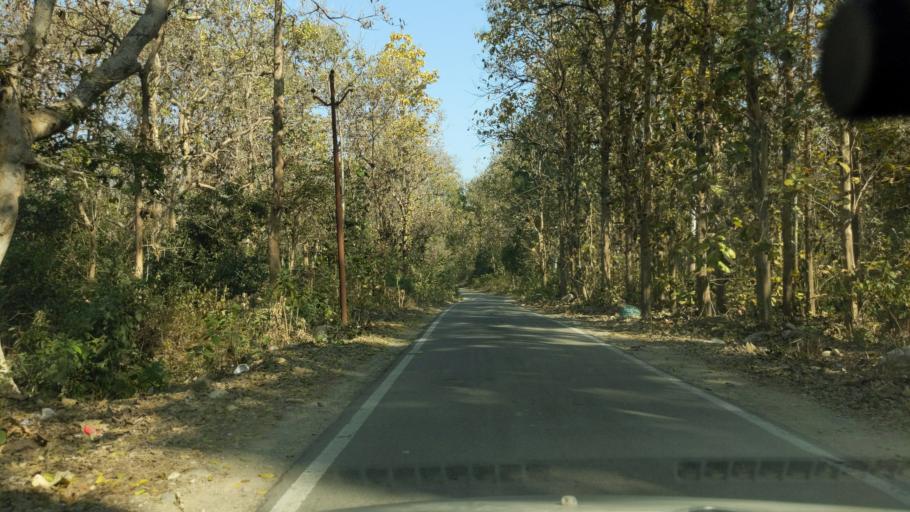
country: IN
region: Uttarakhand
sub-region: Naini Tal
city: Ramnagar
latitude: 29.4031
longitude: 79.1369
